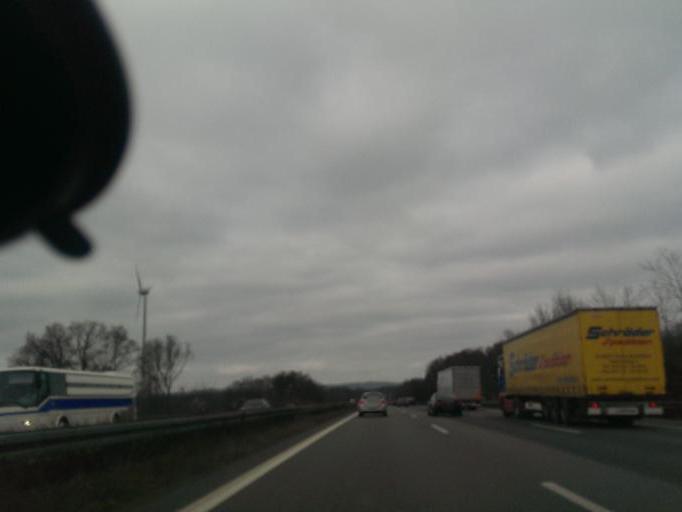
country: DE
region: North Rhine-Westphalia
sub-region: Regierungsbezirk Detmold
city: Verl
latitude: 51.9135
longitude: 8.5150
